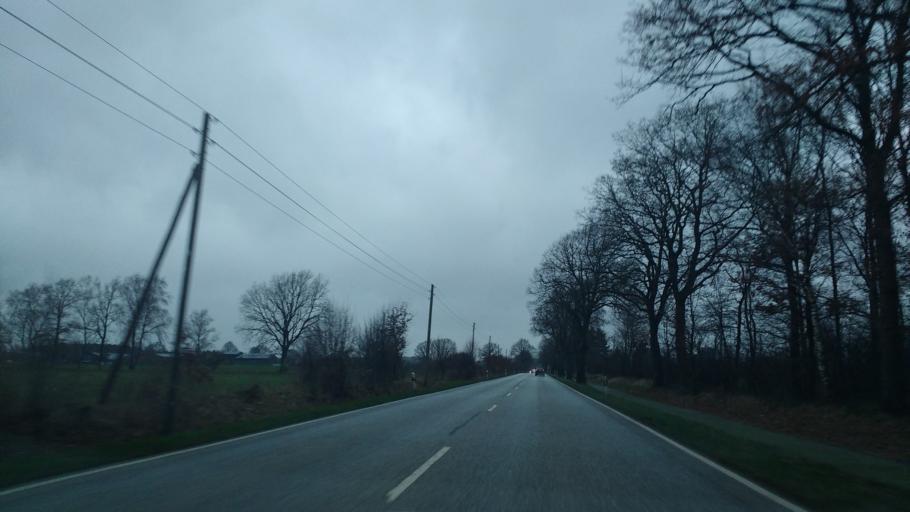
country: DE
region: Schleswig-Holstein
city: Peissen
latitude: 54.0159
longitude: 9.5906
